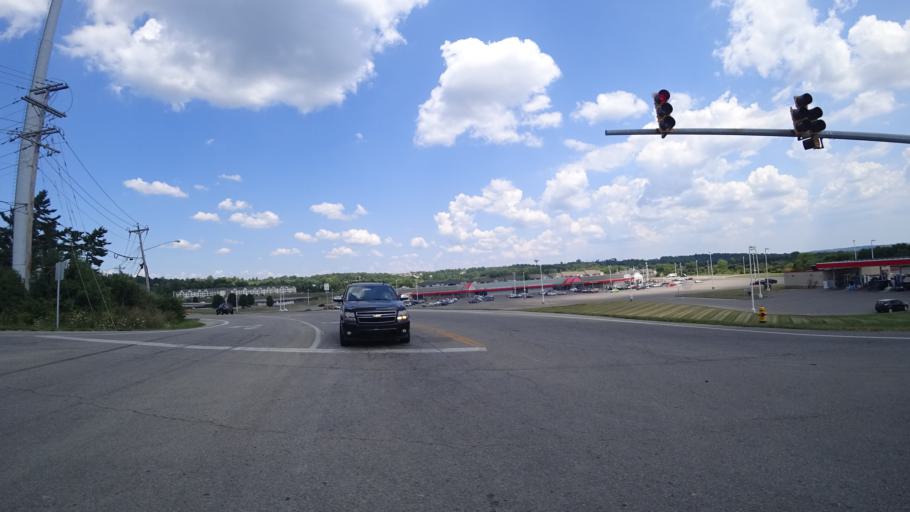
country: US
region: Ohio
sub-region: Butler County
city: Hamilton
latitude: 39.4297
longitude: -84.5998
